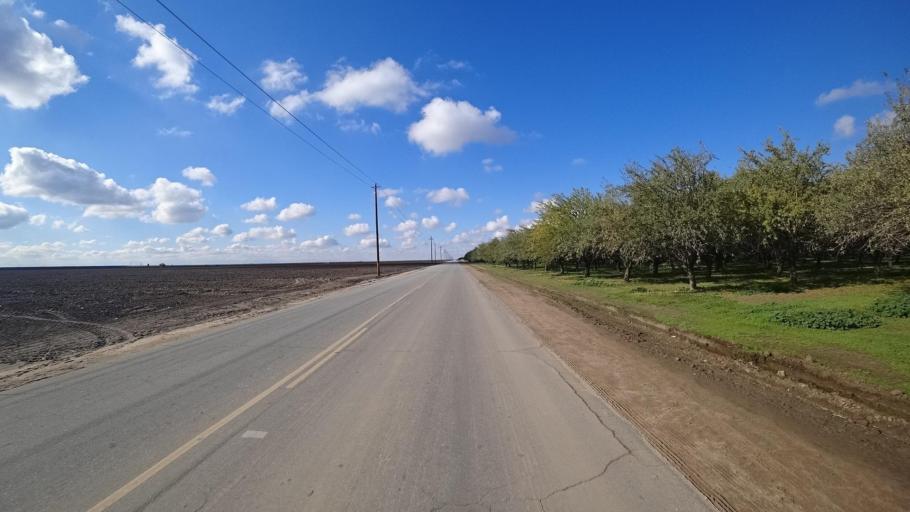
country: US
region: California
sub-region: Kern County
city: McFarland
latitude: 35.6743
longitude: -119.2591
